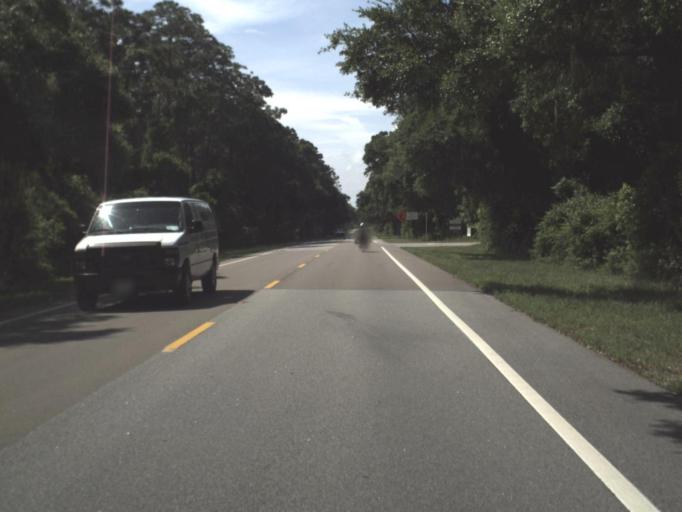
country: US
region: Florida
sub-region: Nassau County
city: Fernandina Beach
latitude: 30.5011
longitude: -81.4512
